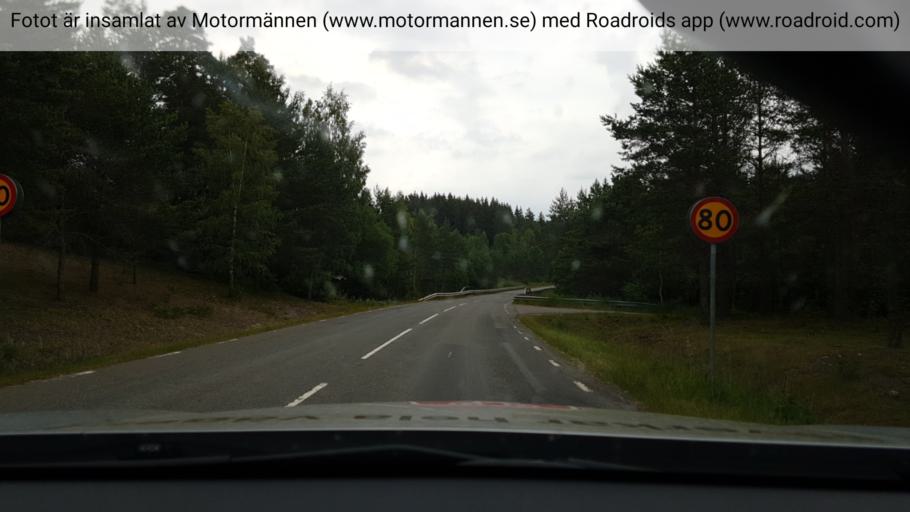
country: SE
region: Joenkoeping
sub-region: Mullsjo Kommun
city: Mullsjoe
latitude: 57.9866
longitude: 13.7823
